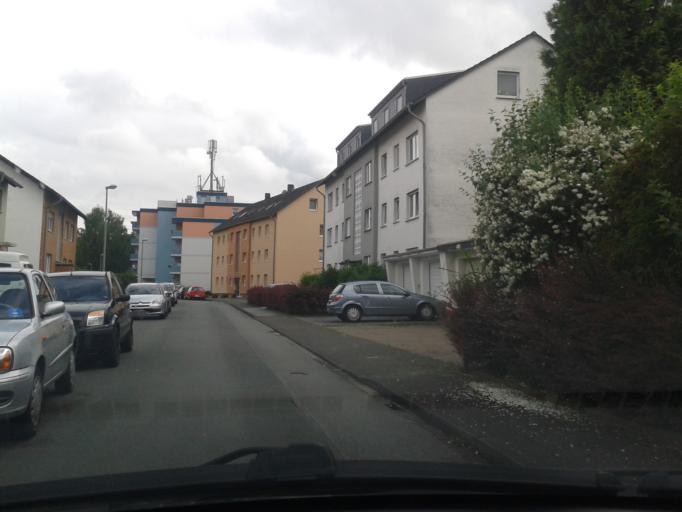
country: DE
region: North Rhine-Westphalia
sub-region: Regierungsbezirk Detmold
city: Paderborn
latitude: 51.7348
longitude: 8.6941
